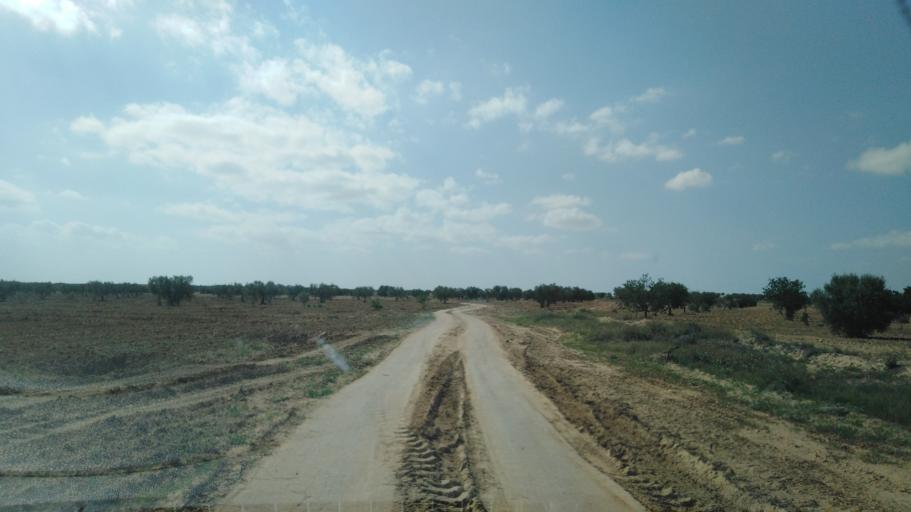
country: TN
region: Safaqis
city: Bi'r `Ali Bin Khalifah
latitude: 34.7982
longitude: 10.3873
